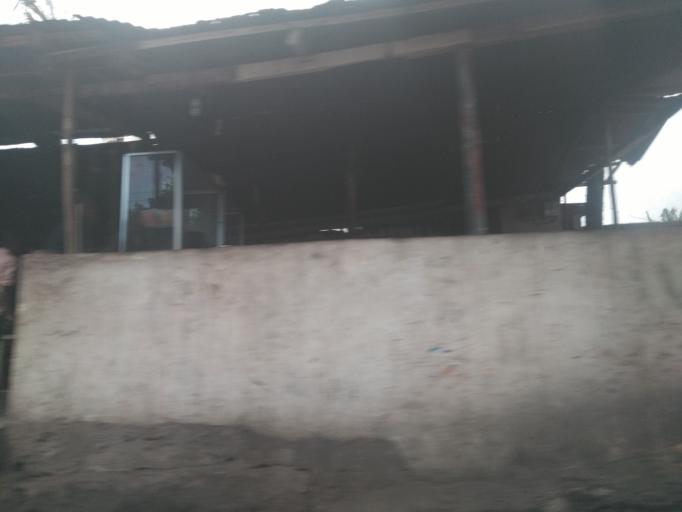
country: TZ
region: Dar es Salaam
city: Magomeni
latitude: -6.7926
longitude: 39.2667
